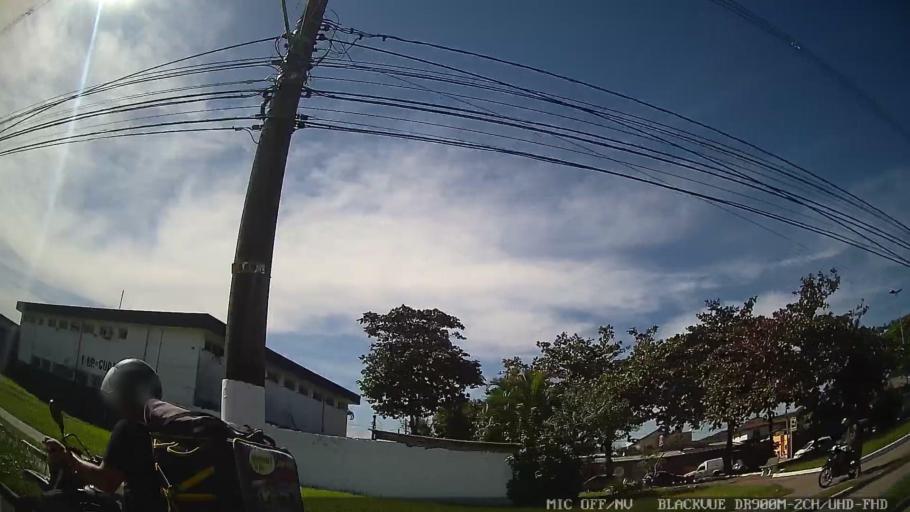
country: BR
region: Sao Paulo
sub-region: Guaruja
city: Guaruja
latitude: -23.9718
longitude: -46.2772
